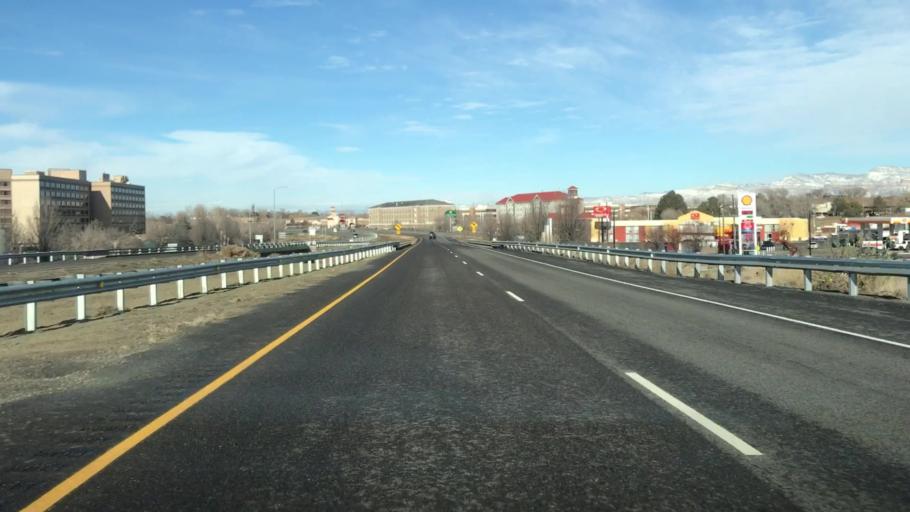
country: US
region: Colorado
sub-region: Mesa County
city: Grand Junction
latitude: 39.1111
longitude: -108.5393
